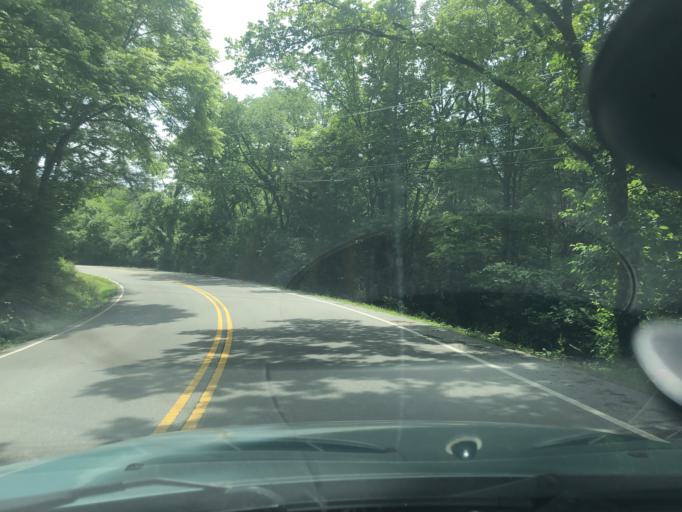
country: US
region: Tennessee
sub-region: Davidson County
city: Lakewood
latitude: 36.1230
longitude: -86.6425
